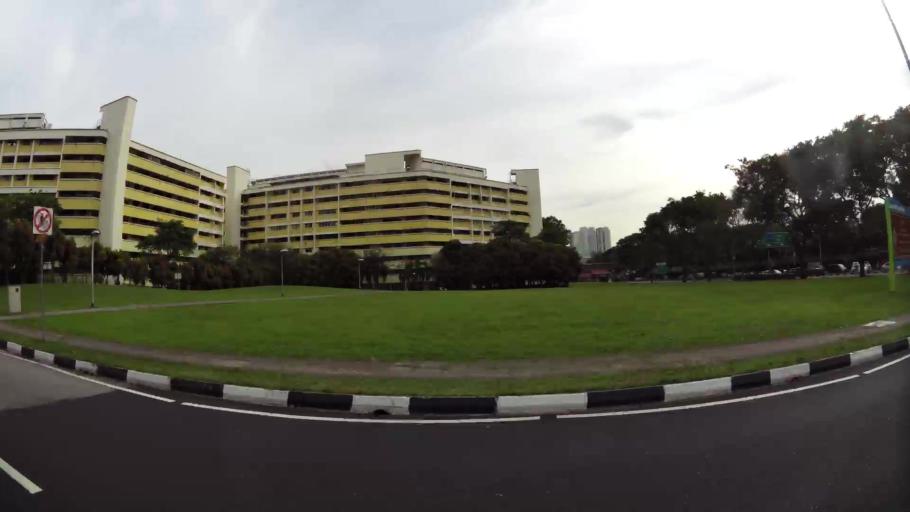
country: SG
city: Singapore
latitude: 1.3483
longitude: 103.8477
